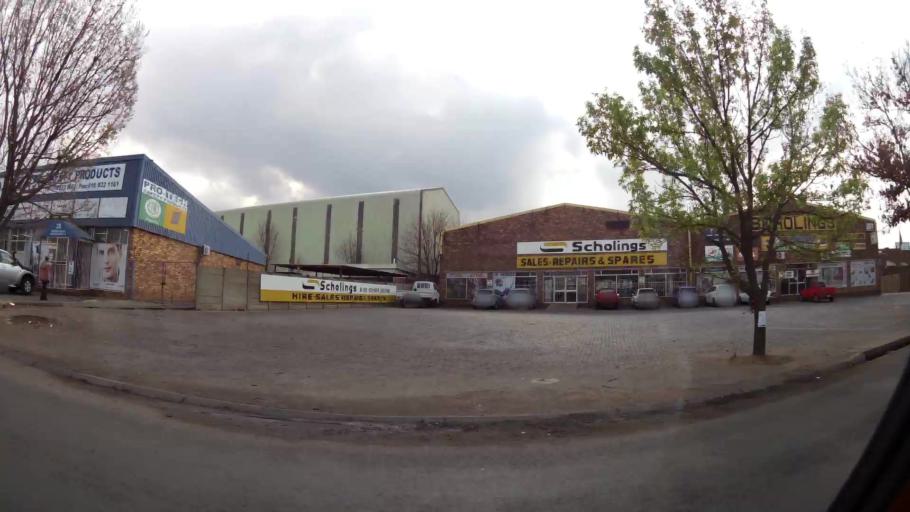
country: ZA
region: Gauteng
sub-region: Sedibeng District Municipality
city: Vanderbijlpark
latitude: -26.7052
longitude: 27.8550
